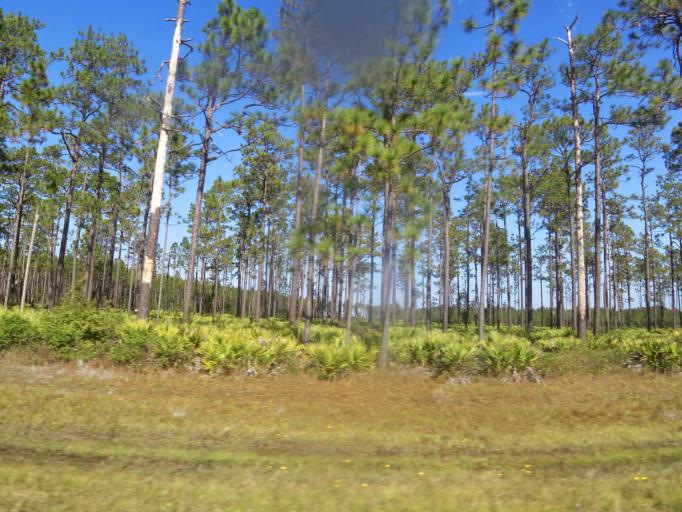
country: US
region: Georgia
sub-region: Charlton County
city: Folkston
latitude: 30.7398
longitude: -82.1004
